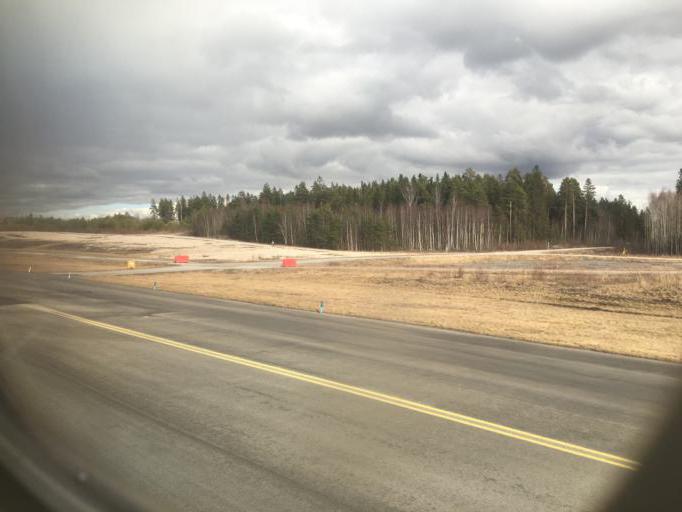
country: SE
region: Stockholm
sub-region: Sigtuna Kommun
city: Marsta
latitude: 59.6632
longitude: 17.9262
